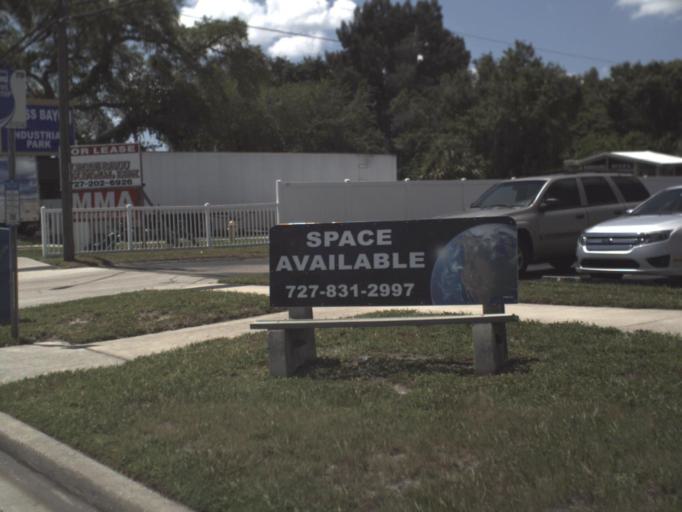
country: US
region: Florida
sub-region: Pinellas County
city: Pinellas Park
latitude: 27.8671
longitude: -82.7290
